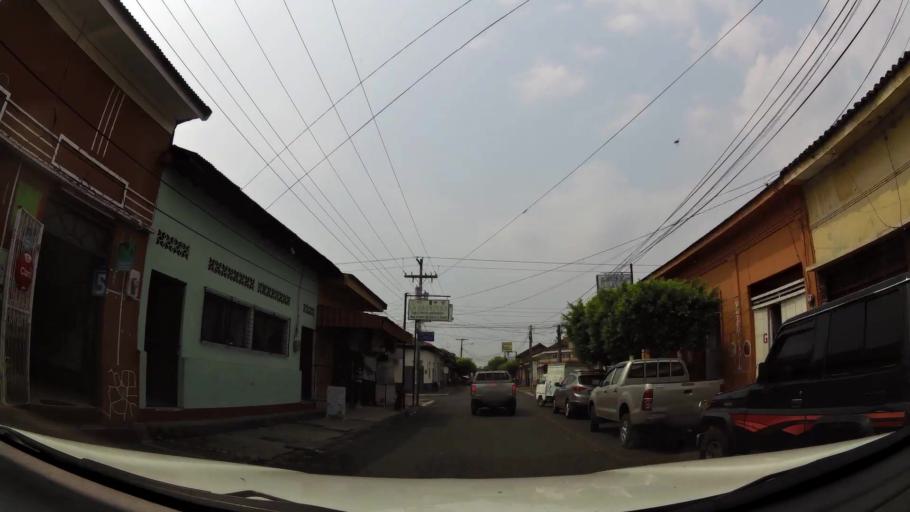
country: NI
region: Chinandega
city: Chinandega
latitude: 12.6332
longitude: -87.1321
